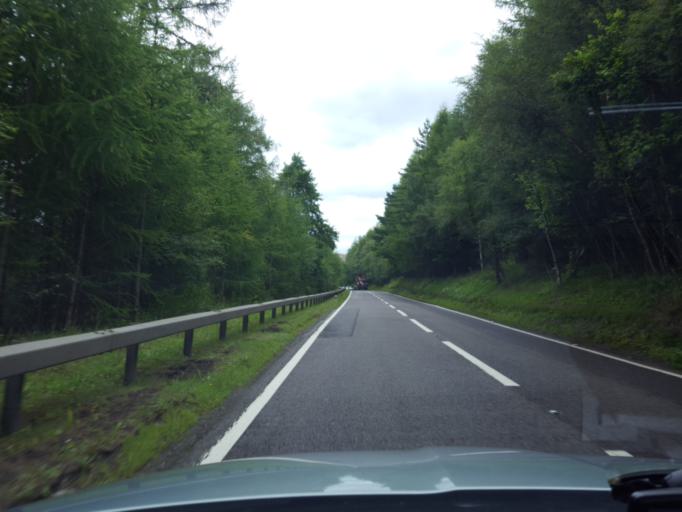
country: GB
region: Scotland
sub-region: Highland
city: Grantown on Spey
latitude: 57.3543
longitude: -3.5221
